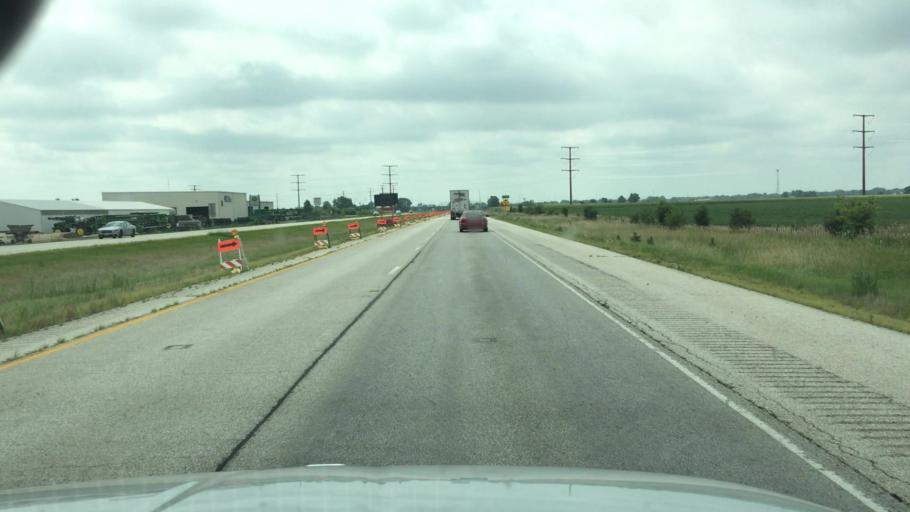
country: US
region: Illinois
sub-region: Knox County
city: Galesburg
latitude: 40.9941
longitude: -90.3360
